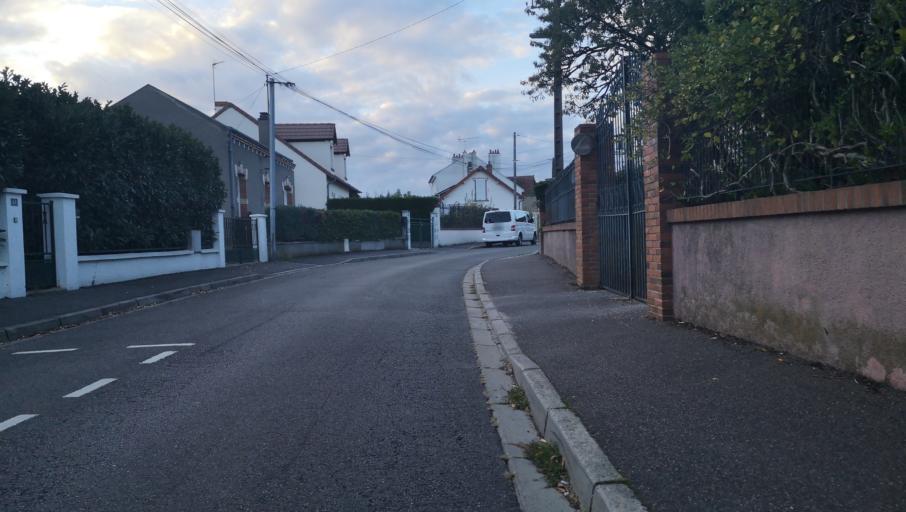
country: FR
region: Centre
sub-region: Departement du Loiret
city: Orleans
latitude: 47.9041
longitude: 1.8847
